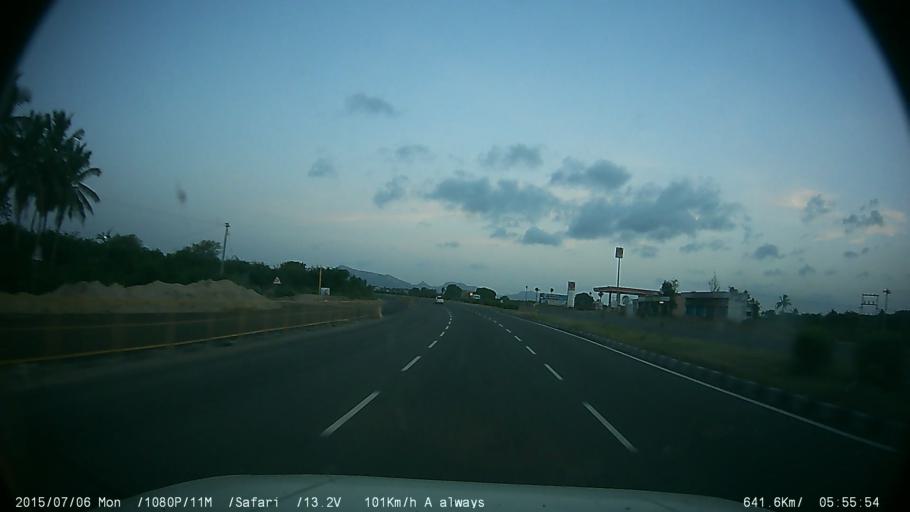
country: IN
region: Tamil Nadu
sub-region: Krishnagiri
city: Krishnagiri
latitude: 12.5684
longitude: 78.1748
